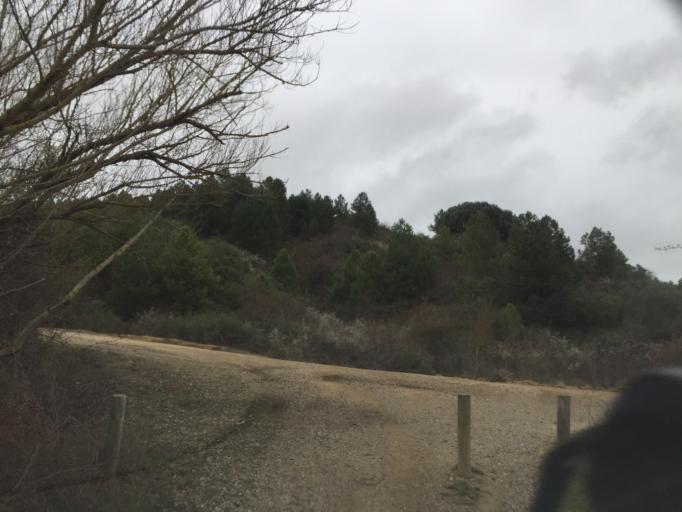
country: ES
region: Castille and Leon
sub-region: Provincia de Leon
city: Leon
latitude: 42.5990
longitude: -5.5407
